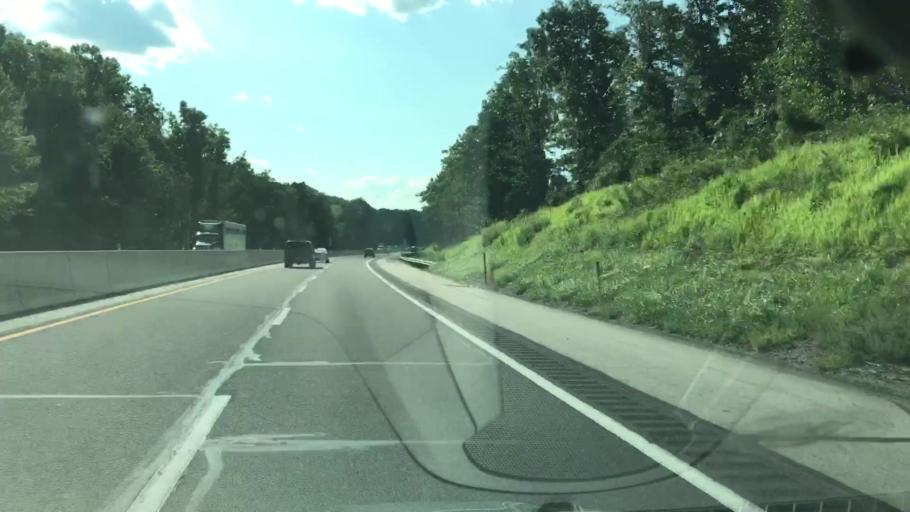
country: US
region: Pennsylvania
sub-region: Lebanon County
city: Cornwall
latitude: 40.2266
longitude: -76.4808
